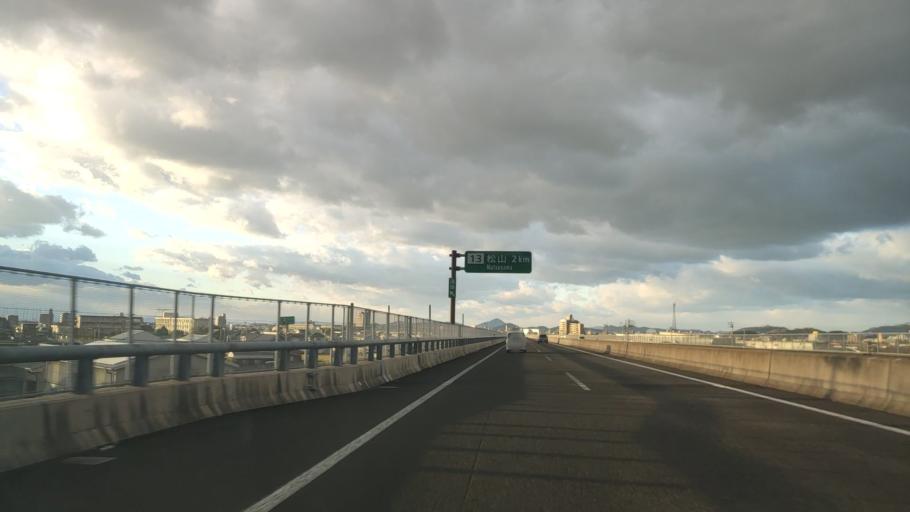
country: JP
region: Ehime
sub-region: Shikoku-chuo Shi
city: Matsuyama
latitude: 33.7916
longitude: 132.8029
